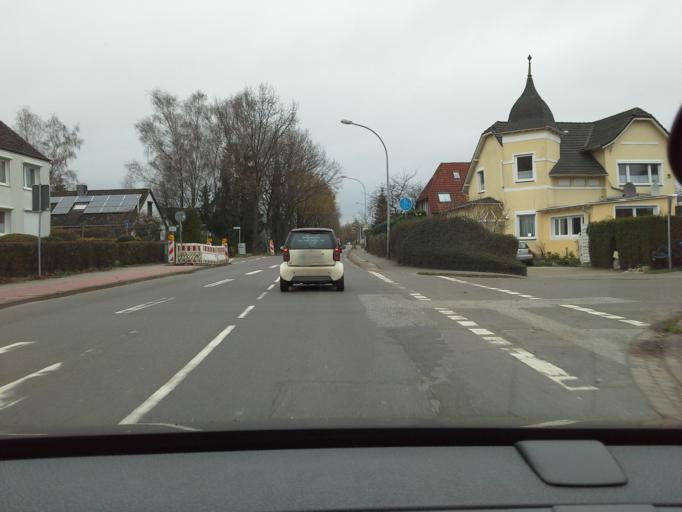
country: DE
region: Schleswig-Holstein
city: Kummerfeld
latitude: 53.6781
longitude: 9.7935
